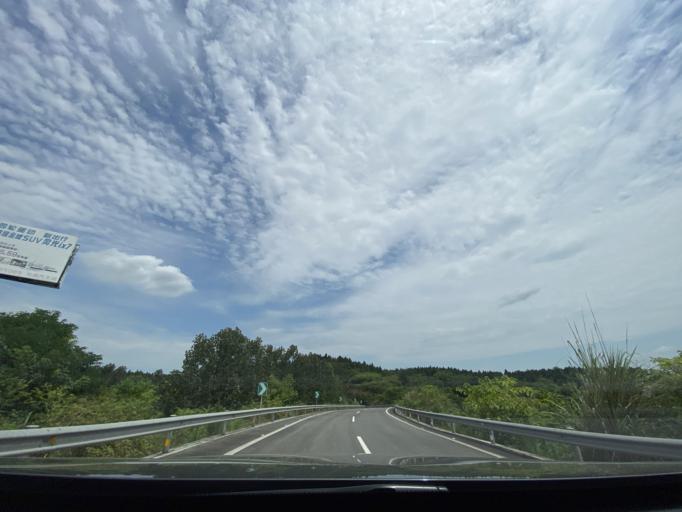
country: CN
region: Sichuan
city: Mianyang
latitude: 31.3507
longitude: 104.7058
